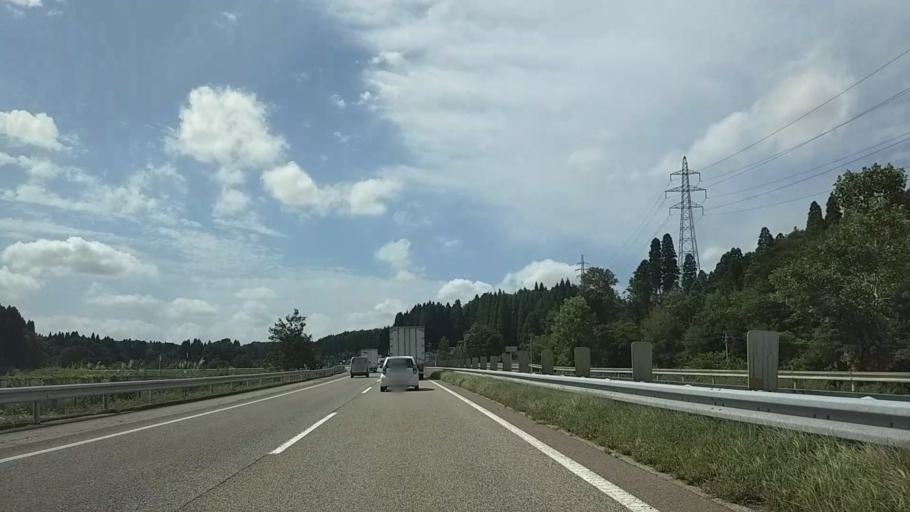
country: JP
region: Toyama
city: Takaoka
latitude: 36.6884
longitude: 137.0611
